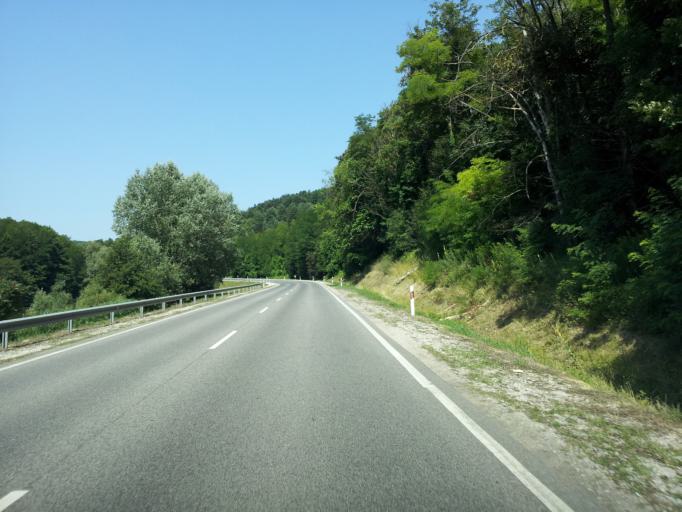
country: HU
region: Zala
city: Heviz
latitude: 46.8083
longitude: 17.0813
